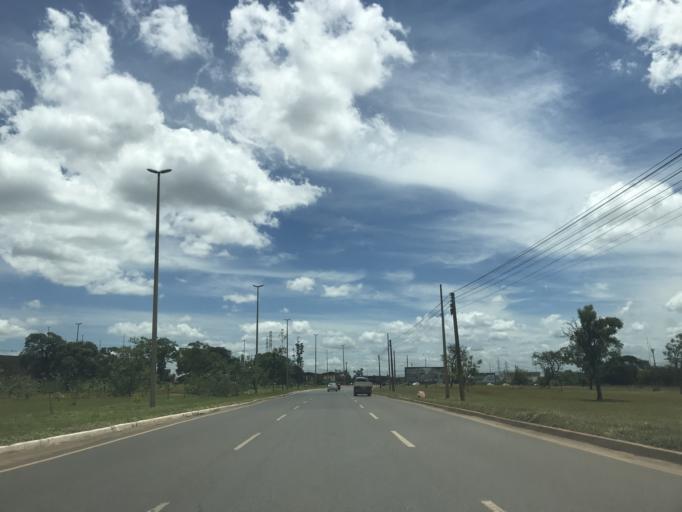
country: BR
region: Federal District
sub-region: Brasilia
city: Brasilia
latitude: -15.7951
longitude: -47.9736
